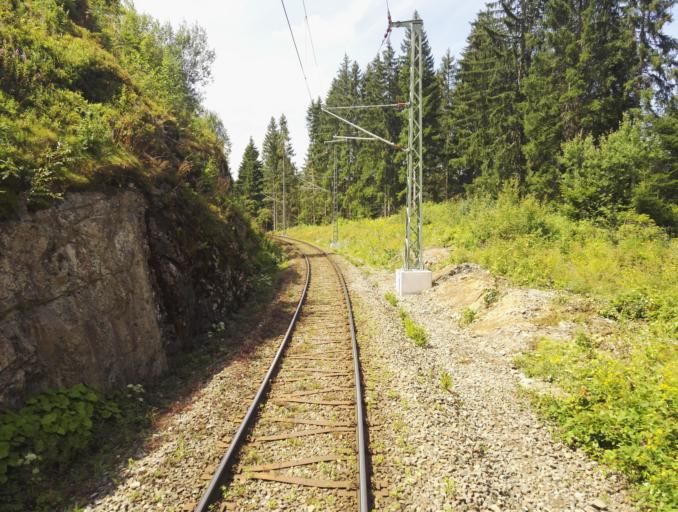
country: DE
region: Baden-Wuerttemberg
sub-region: Freiburg Region
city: Hinterzarten
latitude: 47.8819
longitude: 8.1257
